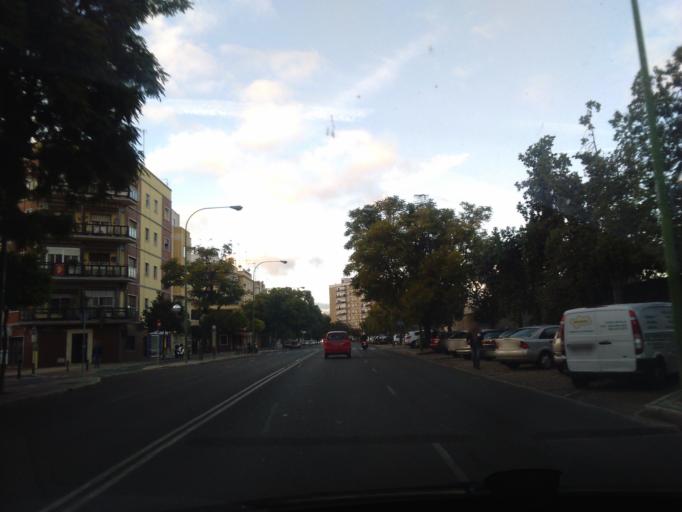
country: ES
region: Andalusia
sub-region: Provincia de Sevilla
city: Sevilla
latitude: 37.3882
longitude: -5.9655
